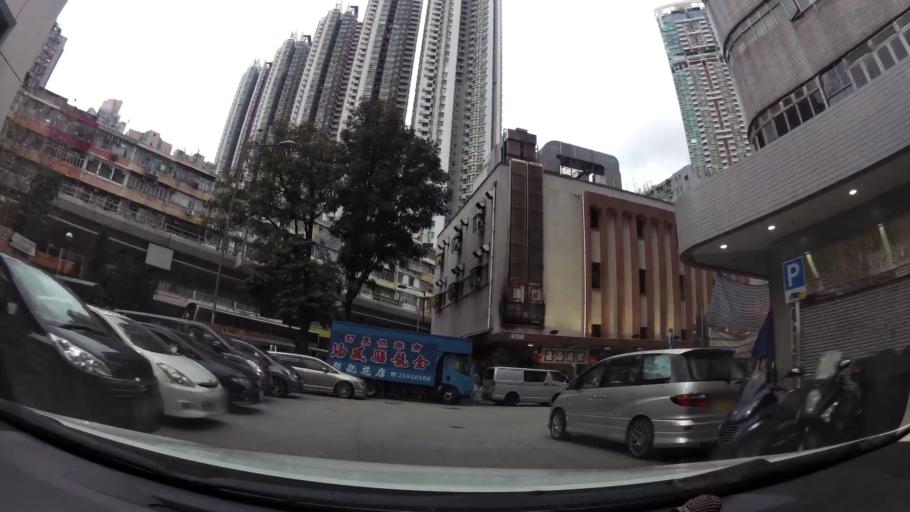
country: HK
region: Sham Shui Po
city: Sham Shui Po
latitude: 22.3236
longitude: 114.1623
